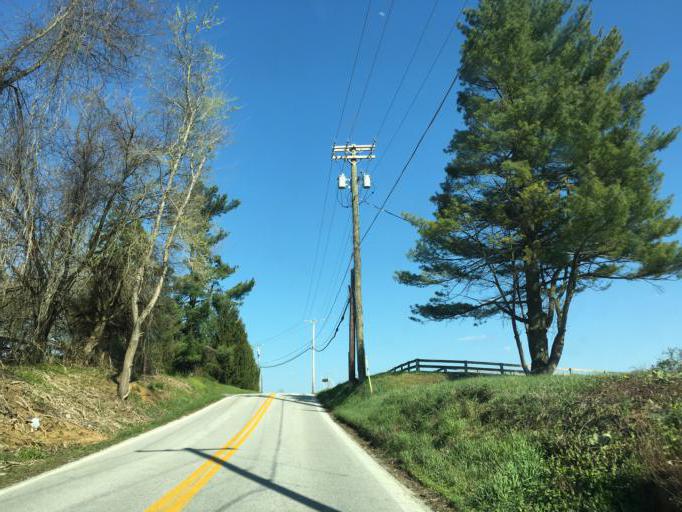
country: US
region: Maryland
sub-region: Baltimore County
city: Hunt Valley
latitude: 39.5415
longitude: -76.6542
